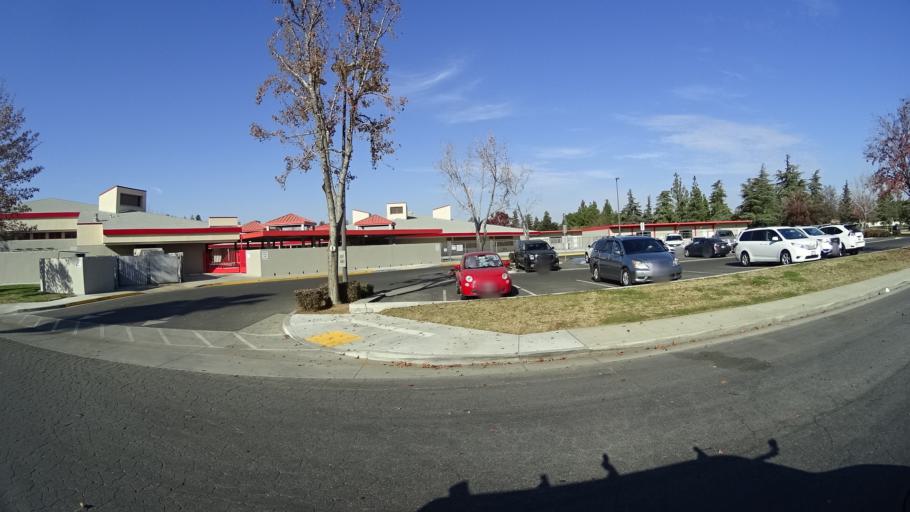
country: US
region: California
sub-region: Kern County
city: Greenacres
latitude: 35.3991
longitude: -119.0857
